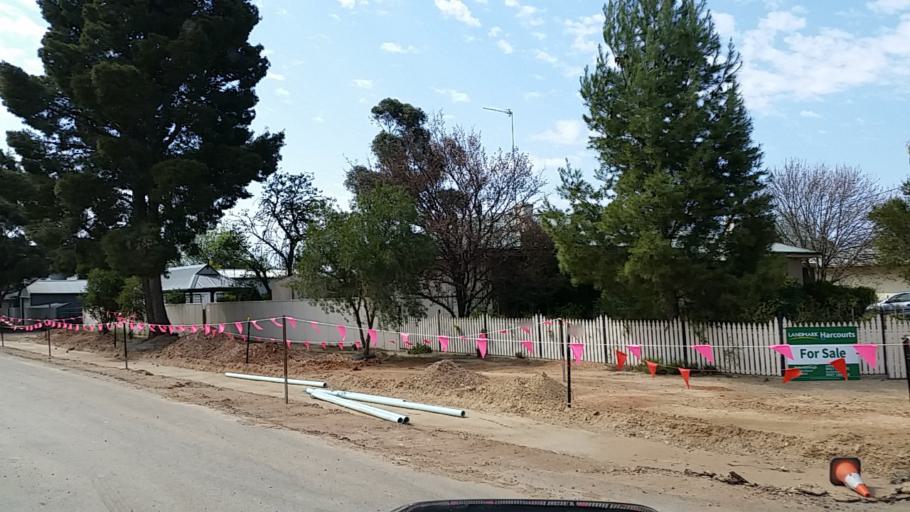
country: AU
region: South Australia
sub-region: Peterborough
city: Peterborough
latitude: -32.9778
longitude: 138.8374
